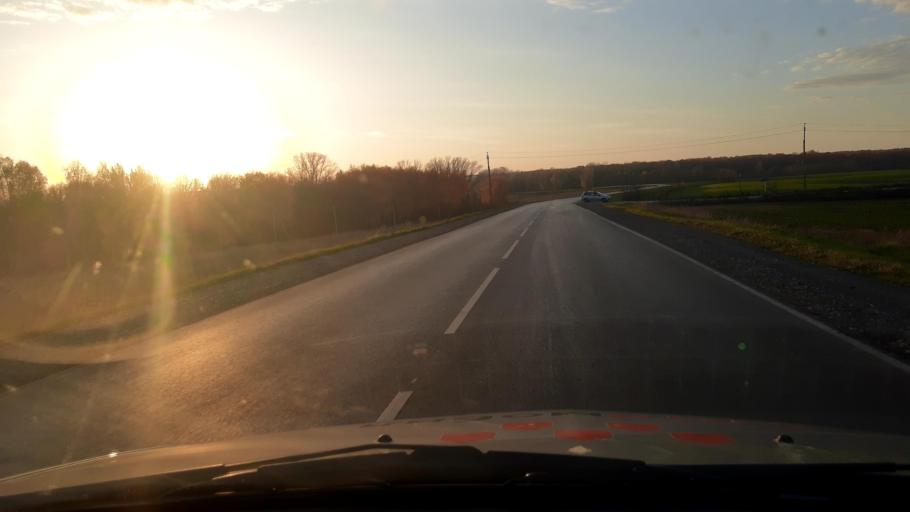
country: RU
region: Bashkortostan
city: Mikhaylovka
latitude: 54.8319
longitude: 55.9469
